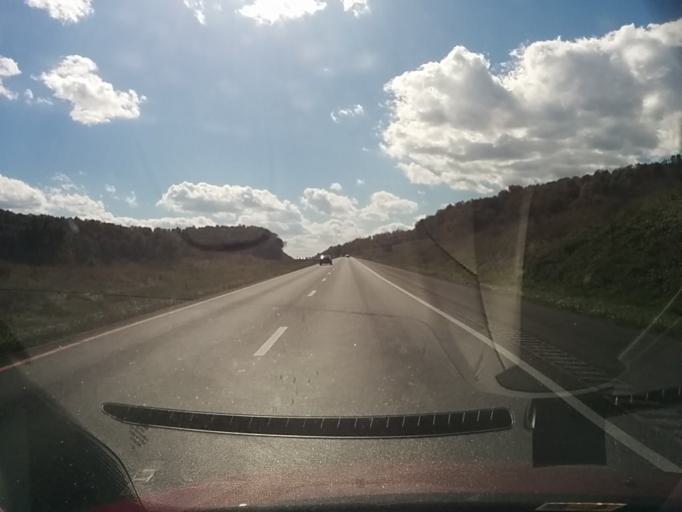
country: US
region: Virginia
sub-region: City of Buena Vista
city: Buena Vista
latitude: 37.9045
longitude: -79.2654
